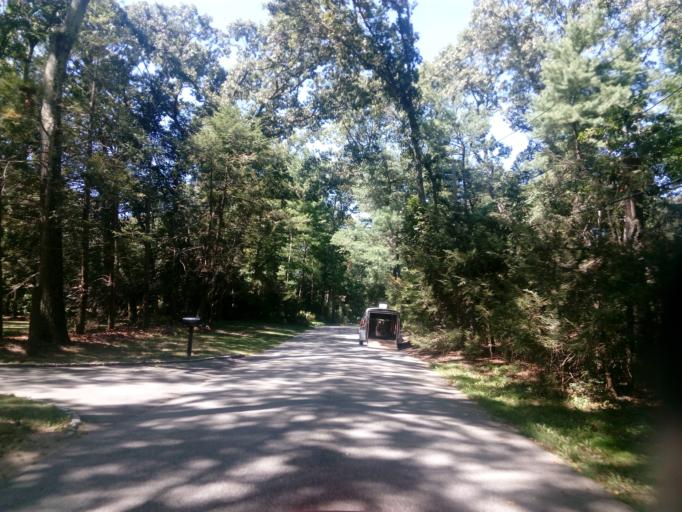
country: US
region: New York
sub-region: Nassau County
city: Upper Brookville
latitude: 40.8437
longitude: -73.5673
